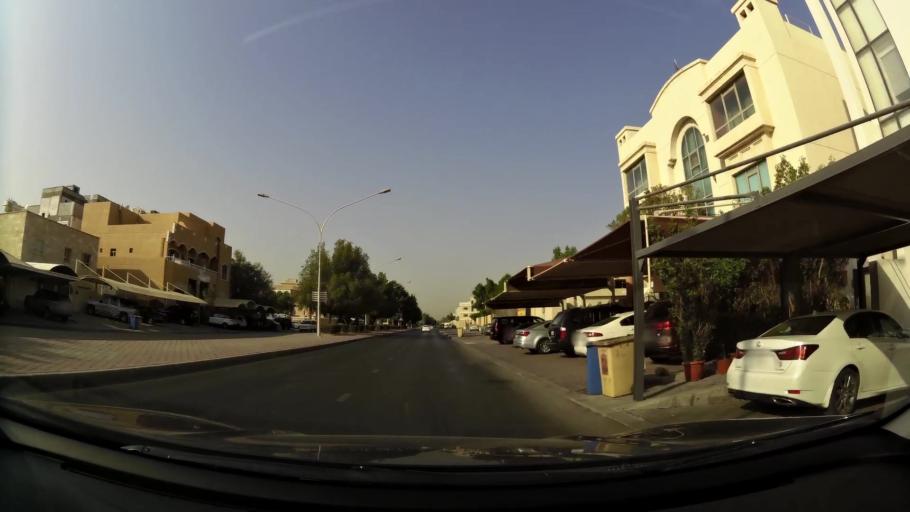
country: KW
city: Bayan
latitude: 29.3196
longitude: 48.0440
